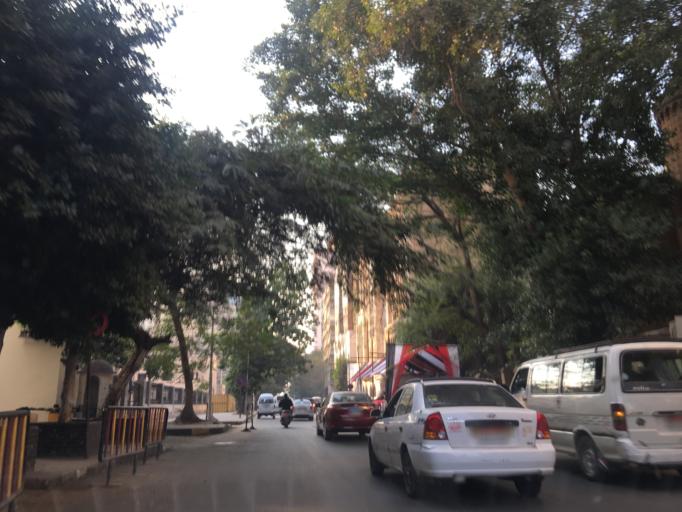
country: EG
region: Muhafazat al Qahirah
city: Cairo
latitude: 30.0416
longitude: 31.2354
